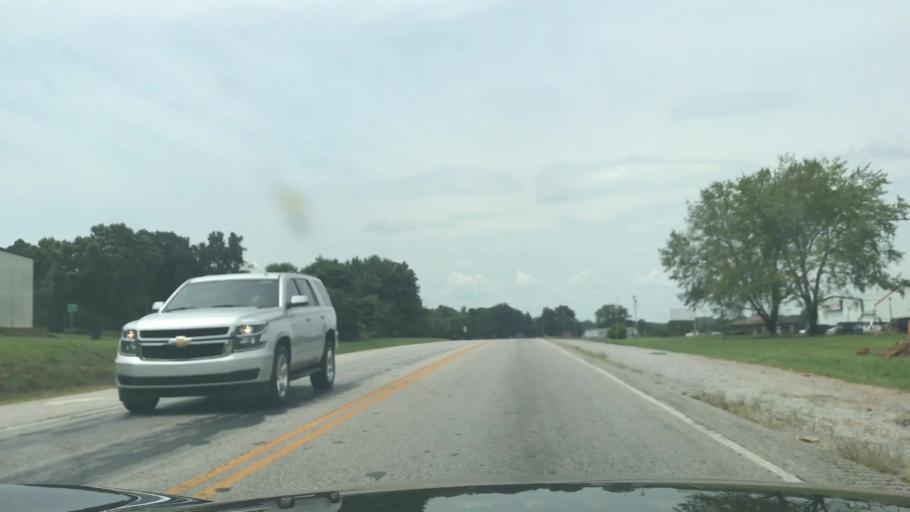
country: US
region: Kentucky
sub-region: Taylor County
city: Campbellsville
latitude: 37.3339
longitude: -85.3756
